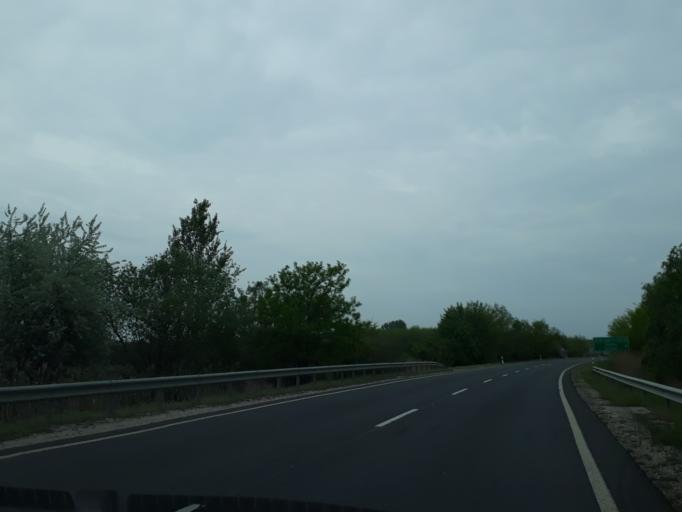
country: HU
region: Szabolcs-Szatmar-Bereg
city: Nyirtass
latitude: 48.0826
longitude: 21.9829
